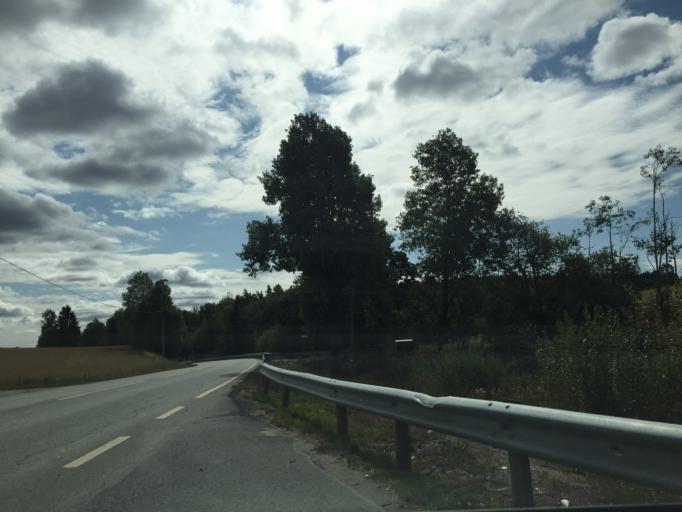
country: NO
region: Ostfold
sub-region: Hobol
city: Elvestad
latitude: 59.6337
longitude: 10.9353
